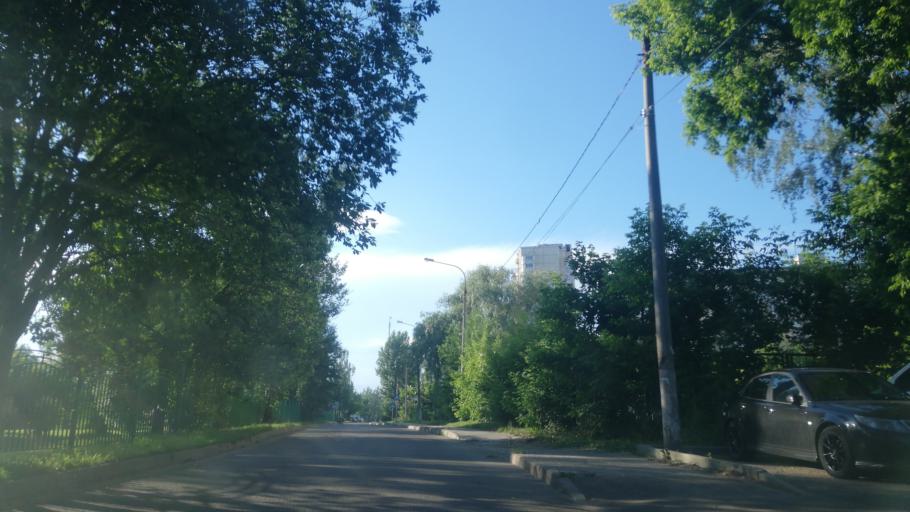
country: RU
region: Moskovskaya
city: Dolgoprudnyy
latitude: 55.9385
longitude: 37.4873
